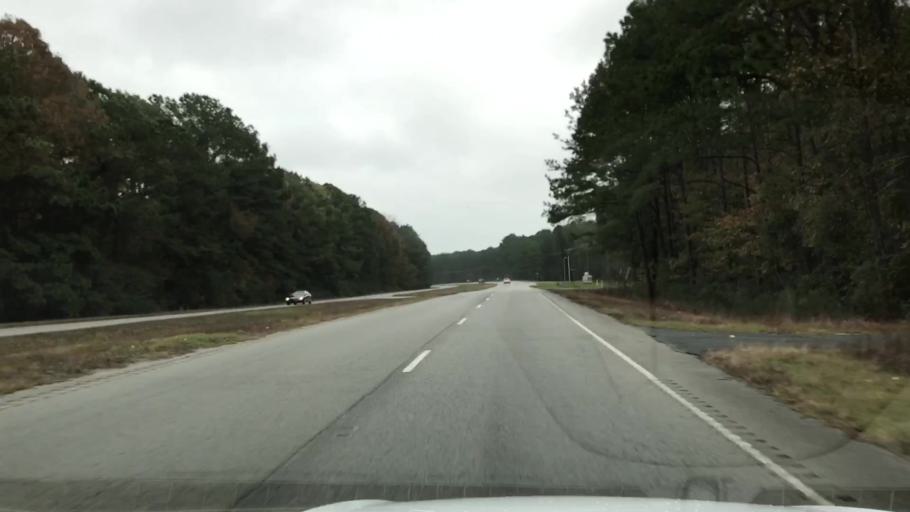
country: US
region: South Carolina
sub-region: Charleston County
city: Awendaw
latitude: 32.9452
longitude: -79.7034
